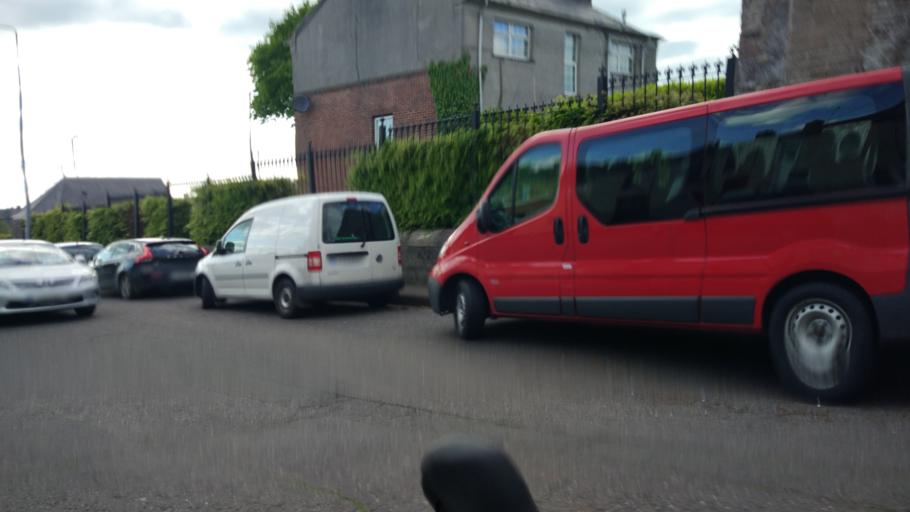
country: IE
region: Munster
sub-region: County Cork
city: Cork
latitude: 51.9064
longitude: -8.4640
